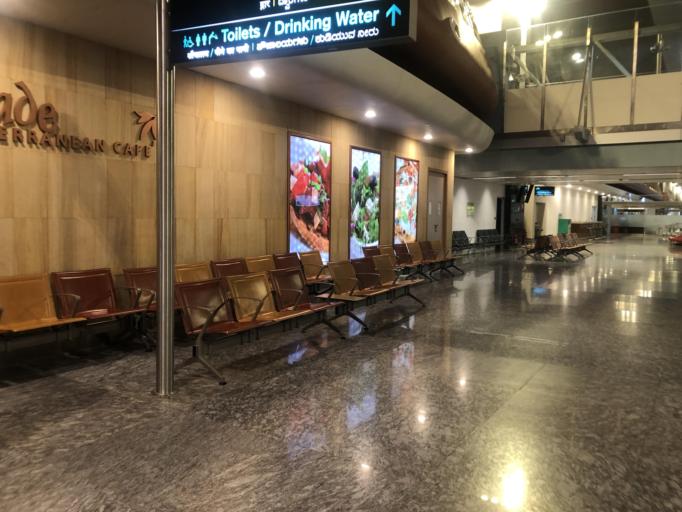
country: IN
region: Karnataka
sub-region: Bangalore Rural
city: Devanhalli
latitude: 13.2012
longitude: 77.7105
